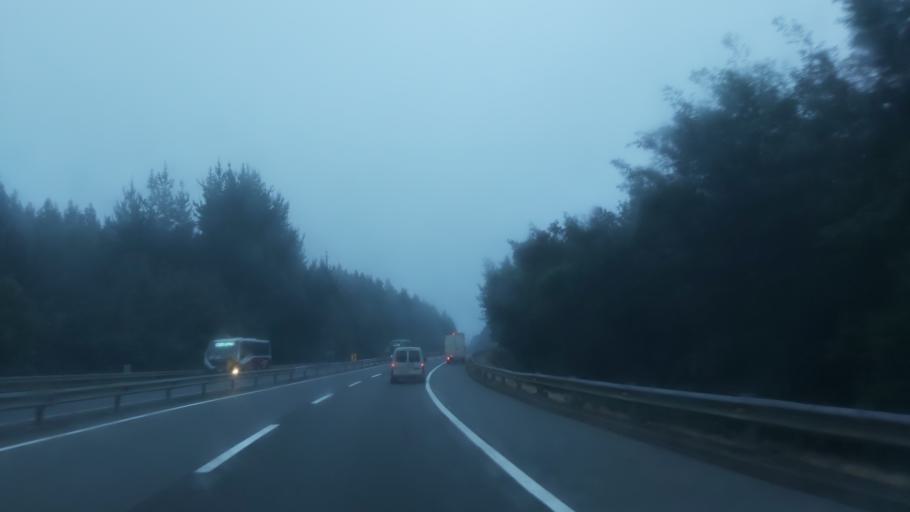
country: CL
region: Biobio
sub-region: Provincia de Concepcion
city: Penco
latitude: -36.7418
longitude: -72.9048
